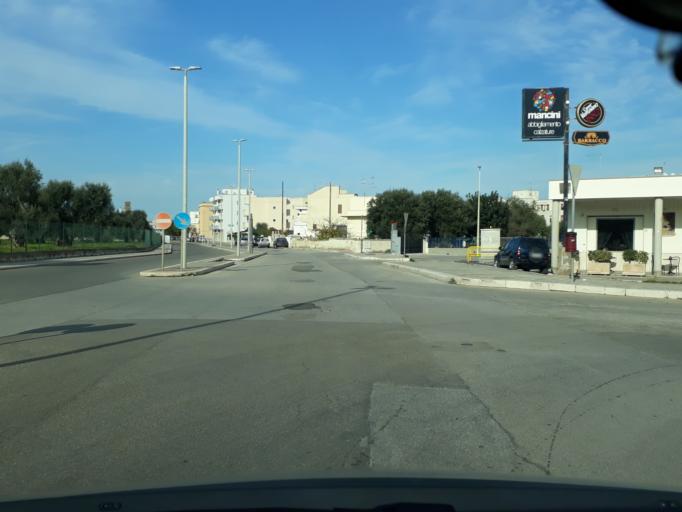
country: IT
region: Apulia
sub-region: Provincia di Brindisi
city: Fasano
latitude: 40.8274
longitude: 17.3606
